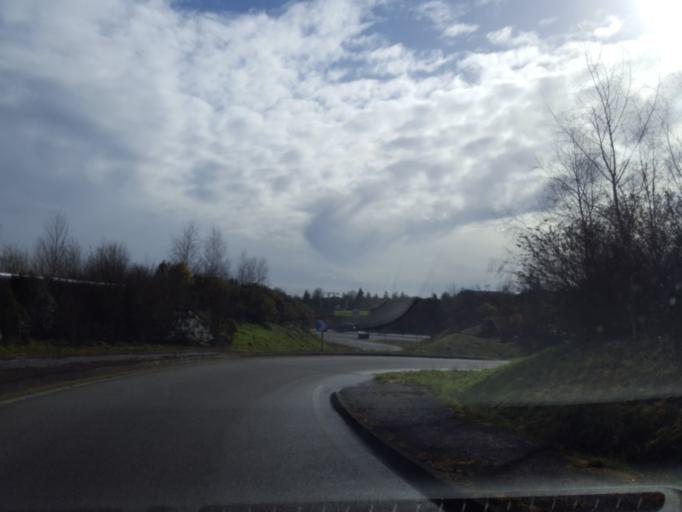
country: FR
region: Brittany
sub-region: Departement d'Ille-et-Vilaine
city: Bruz
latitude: 48.0276
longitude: -1.7678
